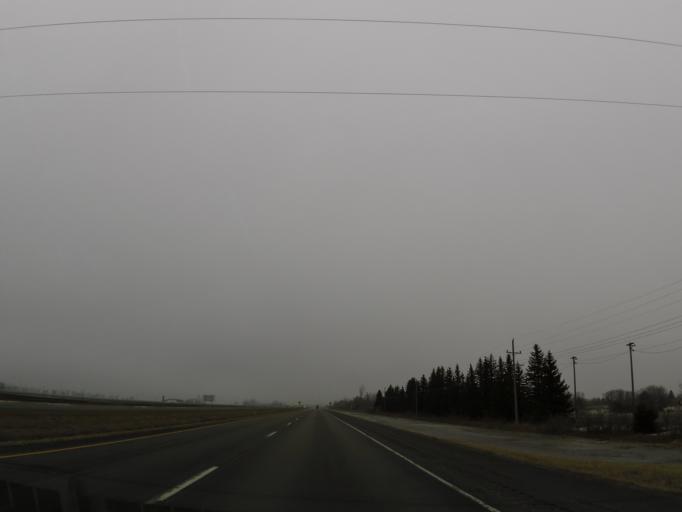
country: US
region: North Dakota
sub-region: Walsh County
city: Grafton
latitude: 48.5567
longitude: -97.1861
